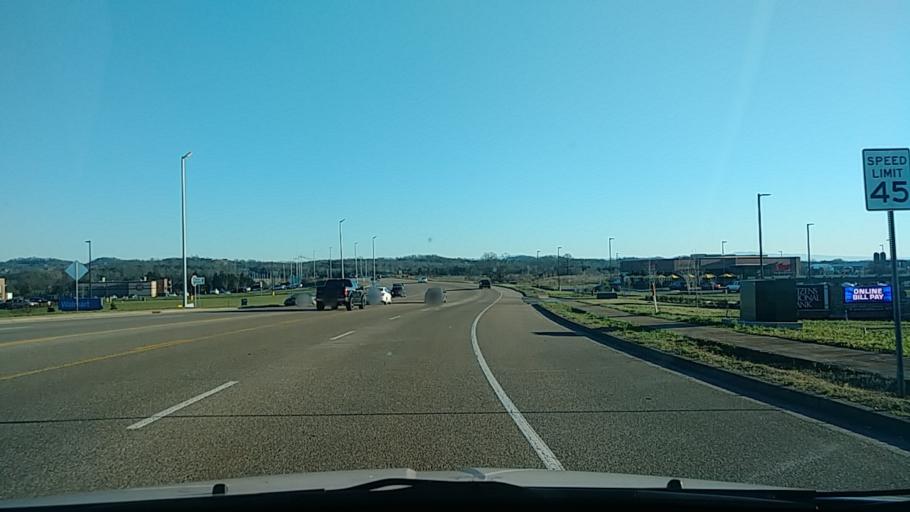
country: US
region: Tennessee
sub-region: Hamblen County
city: Morristown
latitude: 36.1912
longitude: -83.3594
